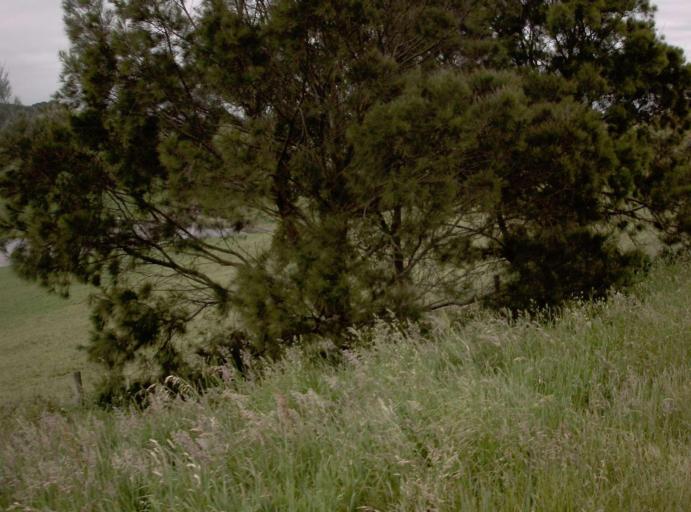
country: AU
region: Victoria
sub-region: Bass Coast
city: North Wonthaggi
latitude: -38.4552
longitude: 145.7951
